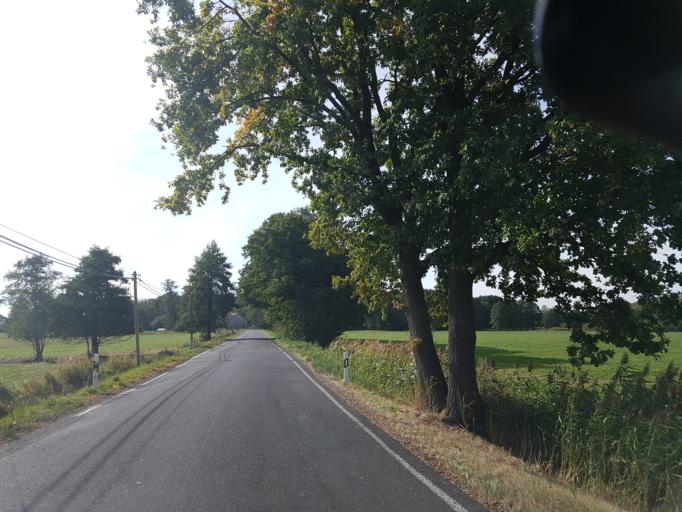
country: DE
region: Brandenburg
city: Schlieben
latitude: 51.7087
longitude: 13.4107
